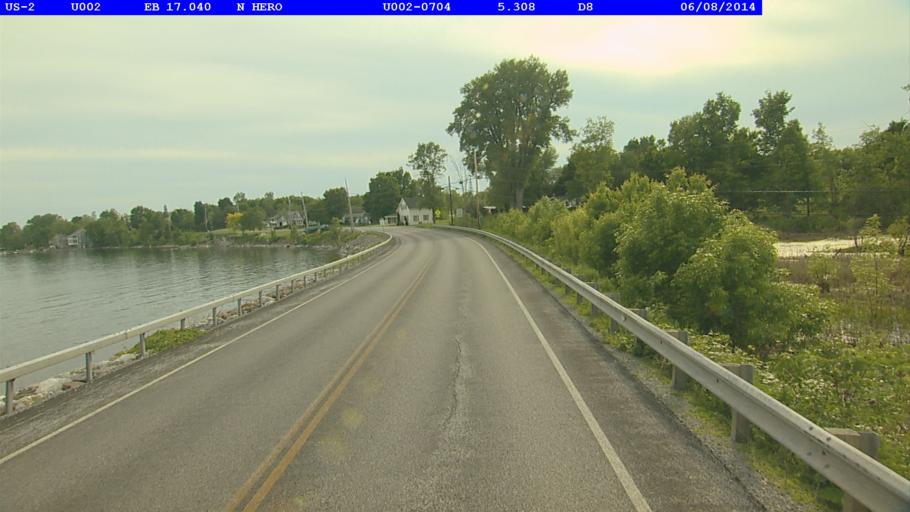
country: US
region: Vermont
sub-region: Grand Isle County
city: North Hero
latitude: 44.8217
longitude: -73.2864
